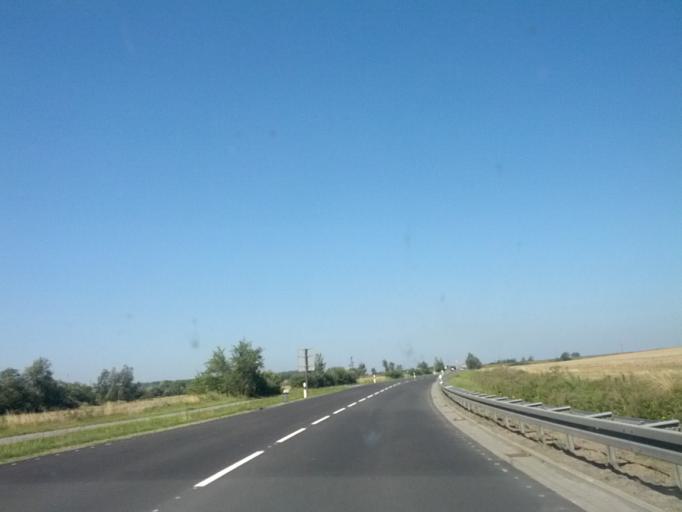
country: DE
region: Mecklenburg-Vorpommern
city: Sagard
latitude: 54.5056
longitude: 13.5463
